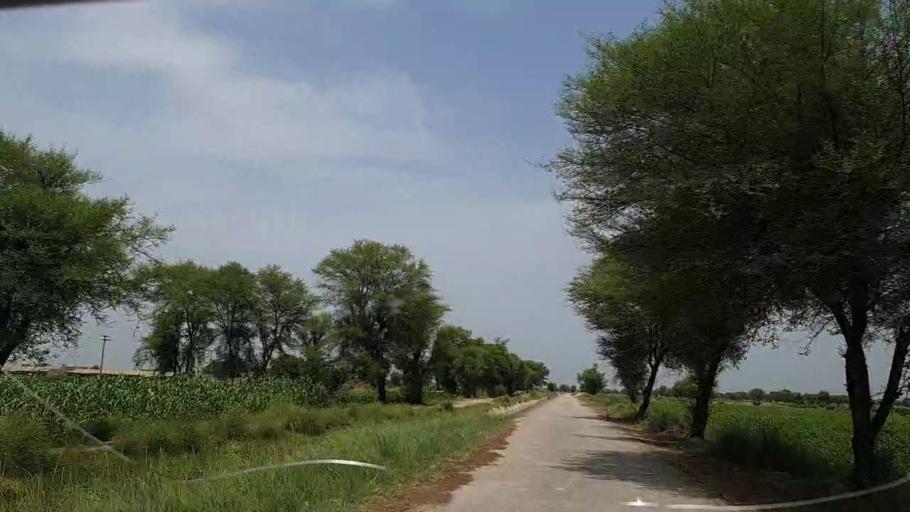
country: PK
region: Sindh
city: Tharu Shah
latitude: 26.9354
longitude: 68.0683
